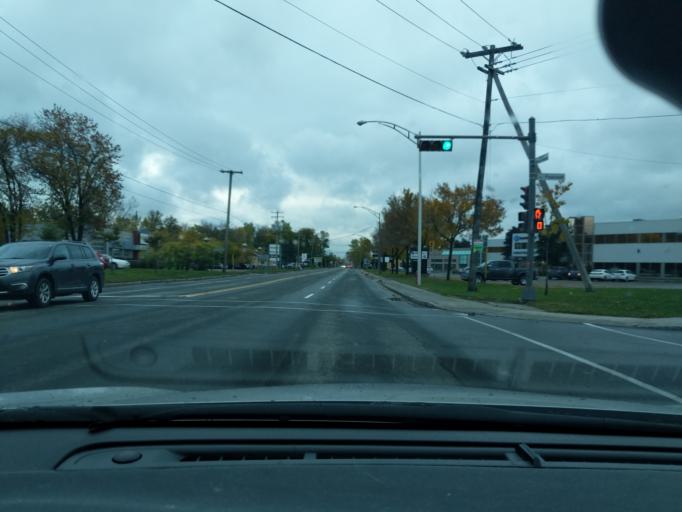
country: CA
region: Quebec
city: L'Ancienne-Lorette
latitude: 46.8062
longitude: -71.3110
